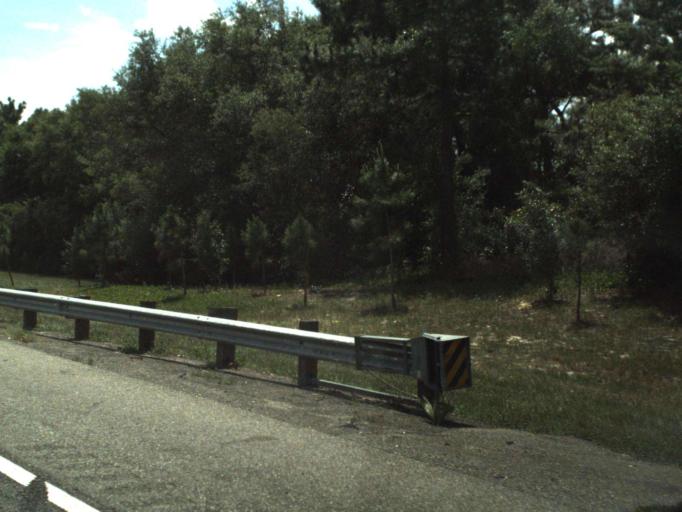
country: US
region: Florida
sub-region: Volusia County
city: Deltona
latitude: 28.9325
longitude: -81.2651
